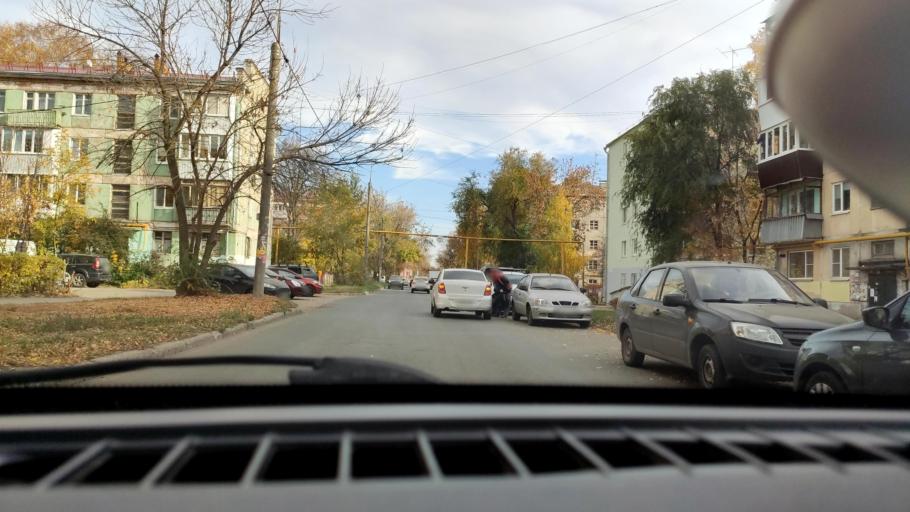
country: RU
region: Samara
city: Petra-Dubrava
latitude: 53.2984
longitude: 50.2830
